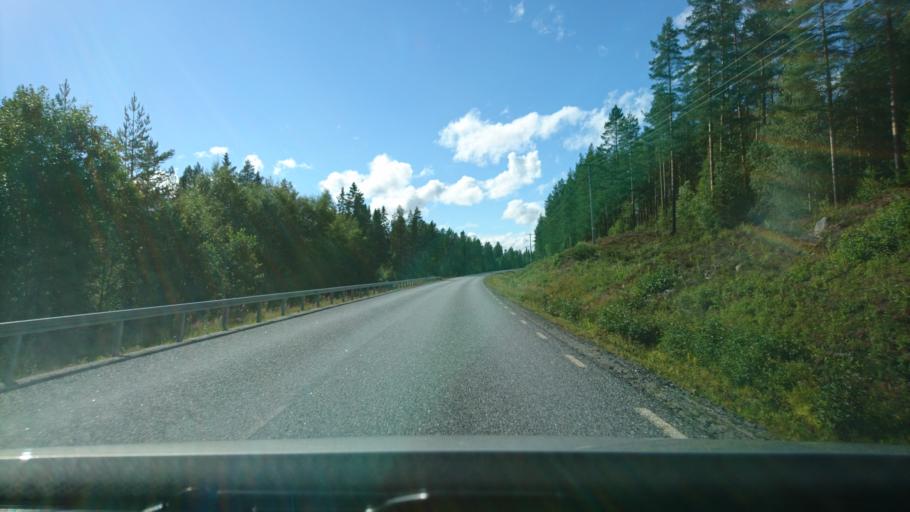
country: SE
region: Vaesterbotten
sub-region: Vilhelmina Kommun
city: Vilhelmina
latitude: 64.3670
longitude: 16.9319
